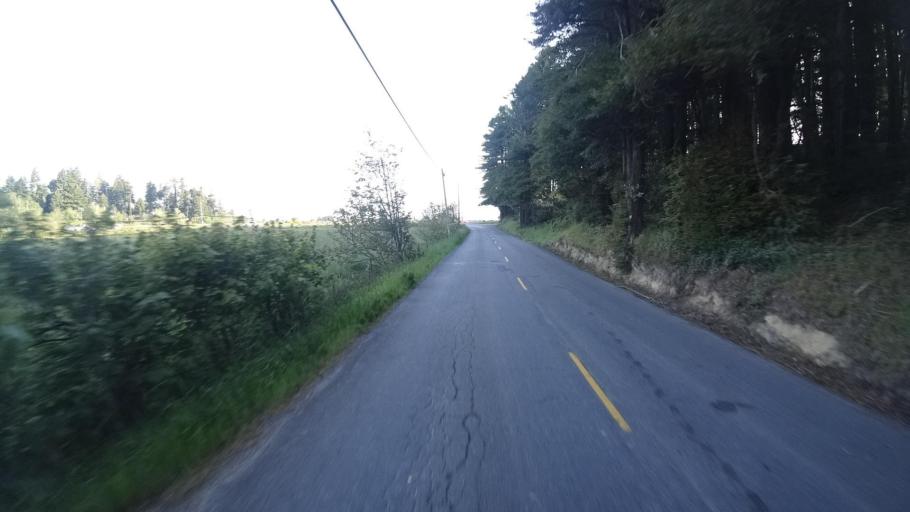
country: US
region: California
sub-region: Humboldt County
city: Myrtletown
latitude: 40.7840
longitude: -124.1185
